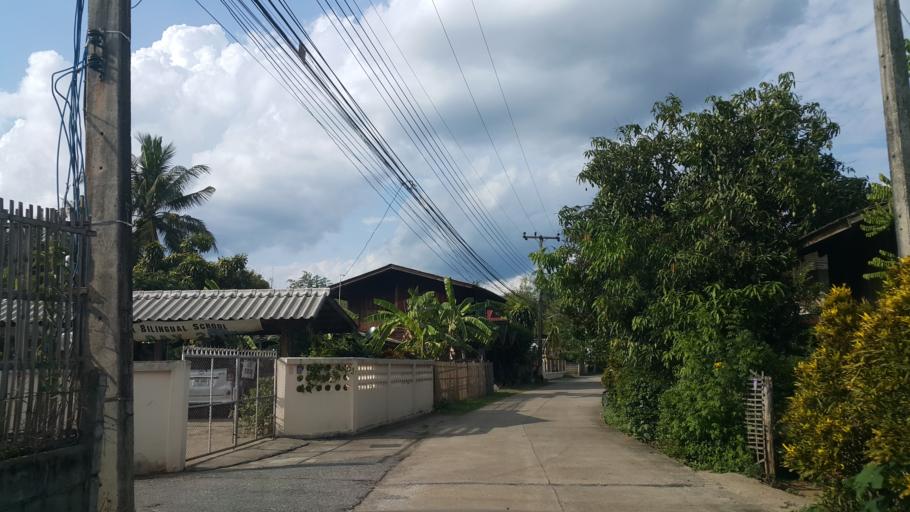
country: TH
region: Chiang Mai
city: Mae On
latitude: 18.7961
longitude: 99.2596
